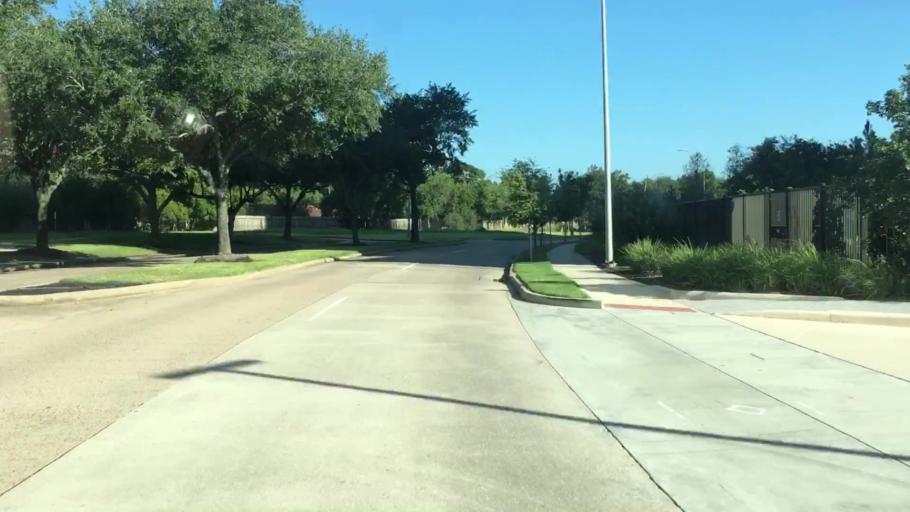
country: US
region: Texas
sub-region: Harris County
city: Bunker Hill Village
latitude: 29.7402
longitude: -95.5618
